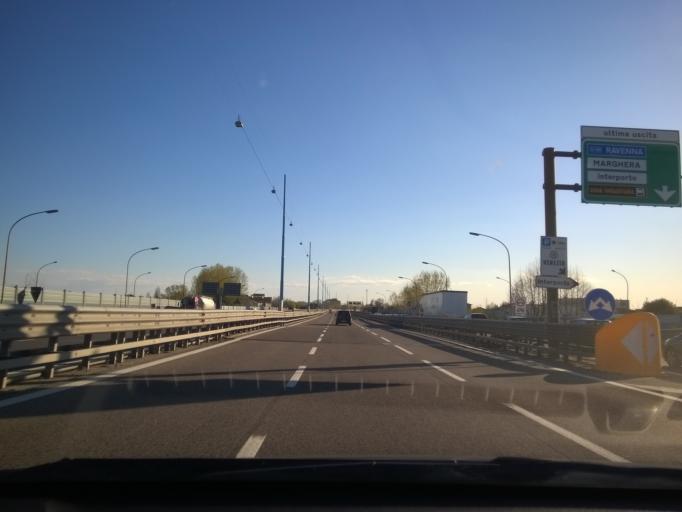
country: IT
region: Veneto
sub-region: Provincia di Venezia
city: Mestre
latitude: 45.4770
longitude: 12.2152
